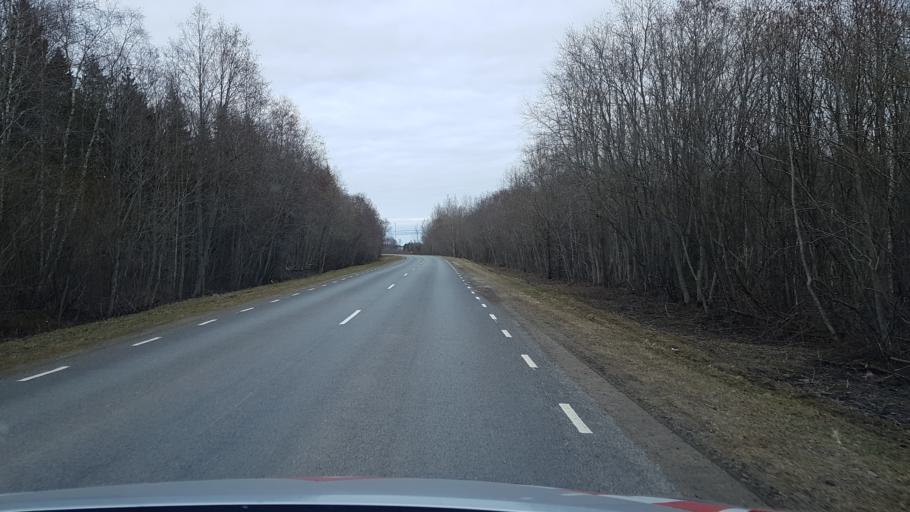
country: EE
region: Ida-Virumaa
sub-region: Sillamaee linn
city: Sillamae
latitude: 59.3606
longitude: 27.7544
